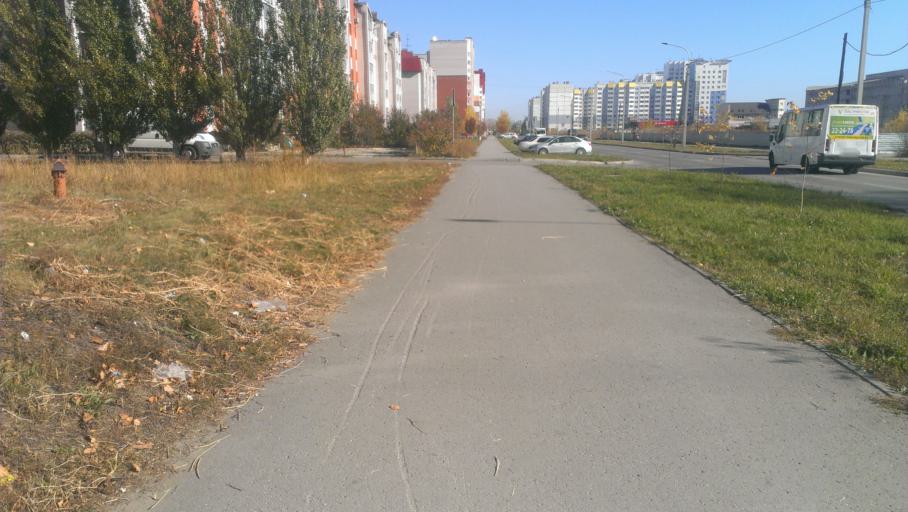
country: RU
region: Altai Krai
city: Novosilikatnyy
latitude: 53.3306
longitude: 83.6785
